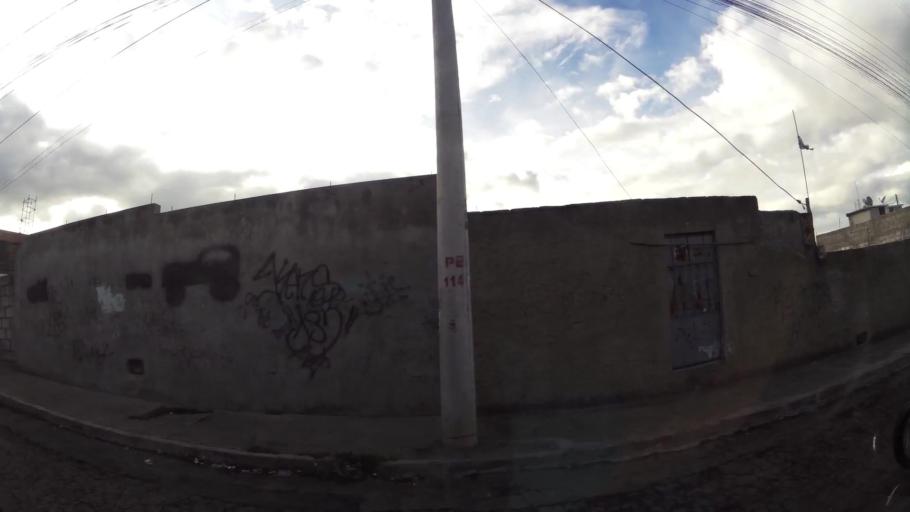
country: EC
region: Pichincha
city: Quito
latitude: -0.1349
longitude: -78.4593
